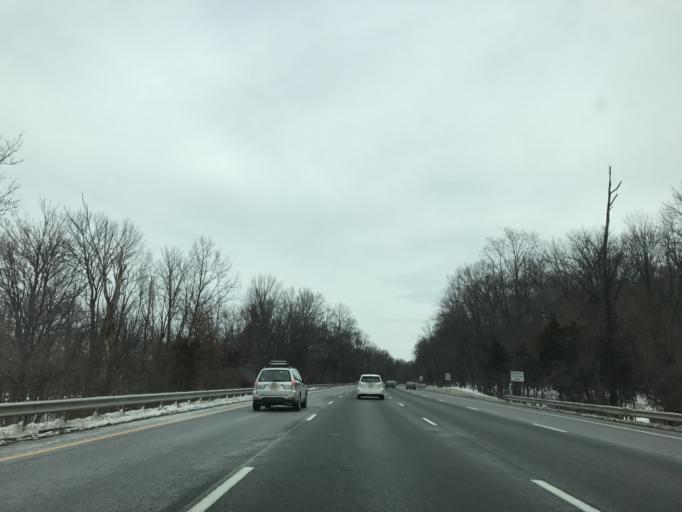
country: US
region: New Jersey
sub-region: Somerset County
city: Bedminster
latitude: 40.6653
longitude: -74.6384
